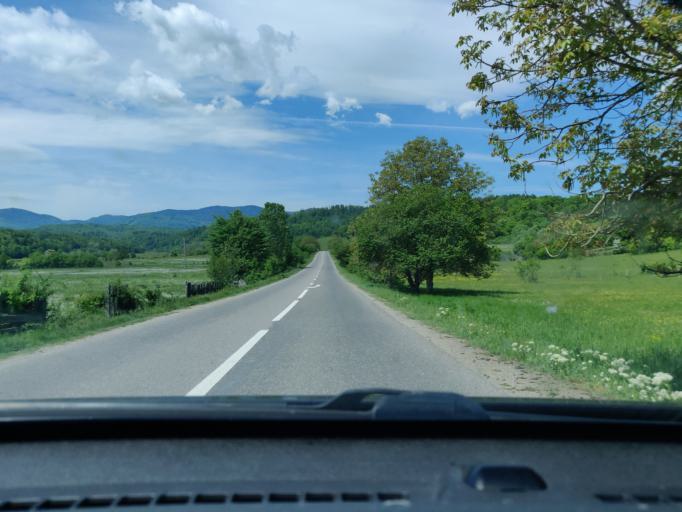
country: RO
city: Campurile de Jos
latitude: 46.0423
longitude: 26.7289
